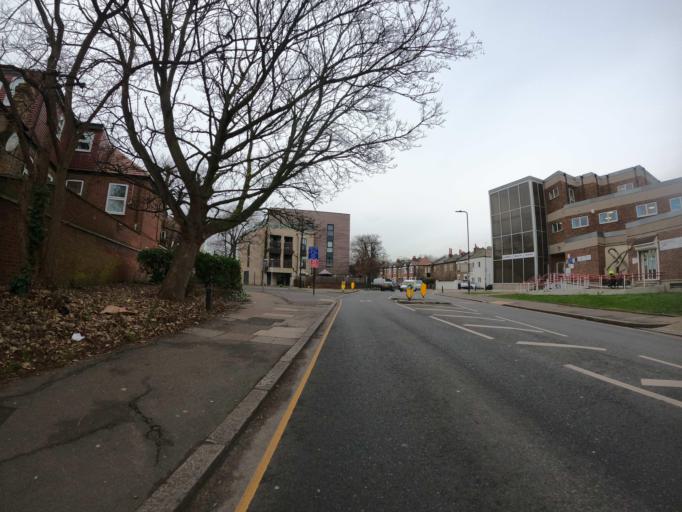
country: GB
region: England
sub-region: Greater London
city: Greenford
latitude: 51.5100
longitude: -0.3347
